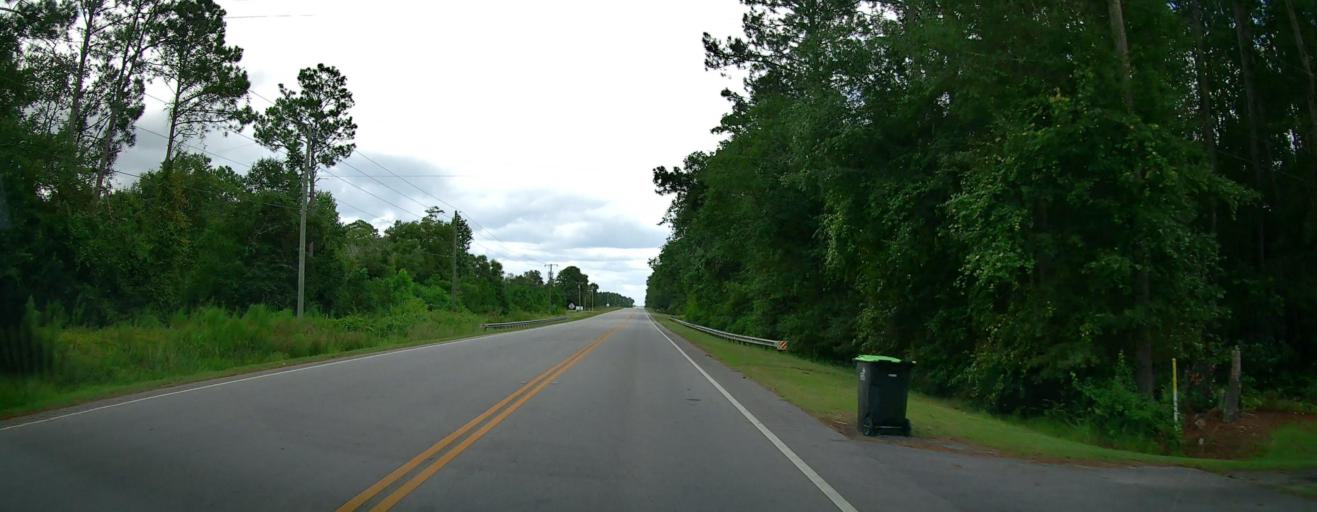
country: US
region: Georgia
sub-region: Coffee County
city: Broxton
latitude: 31.5710
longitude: -83.0247
